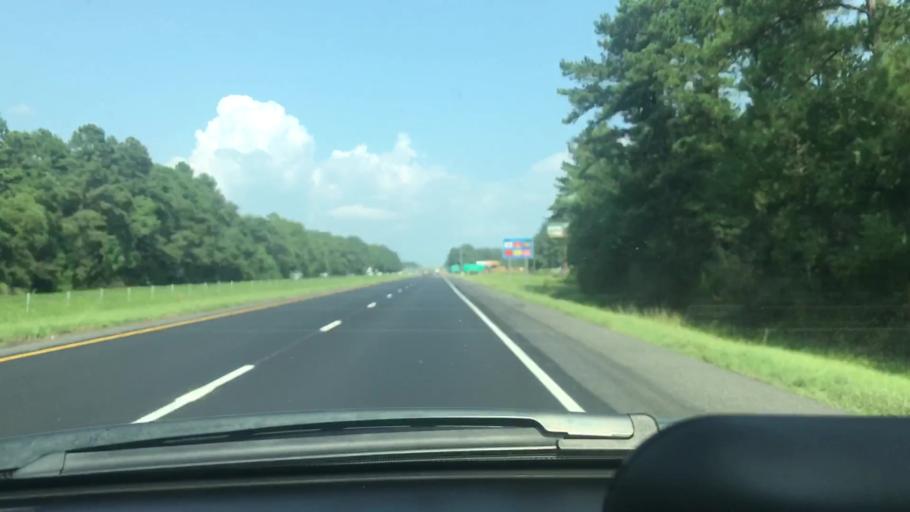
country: US
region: Louisiana
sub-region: Tangipahoa Parish
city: Hammond
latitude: 30.4788
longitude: -90.4749
